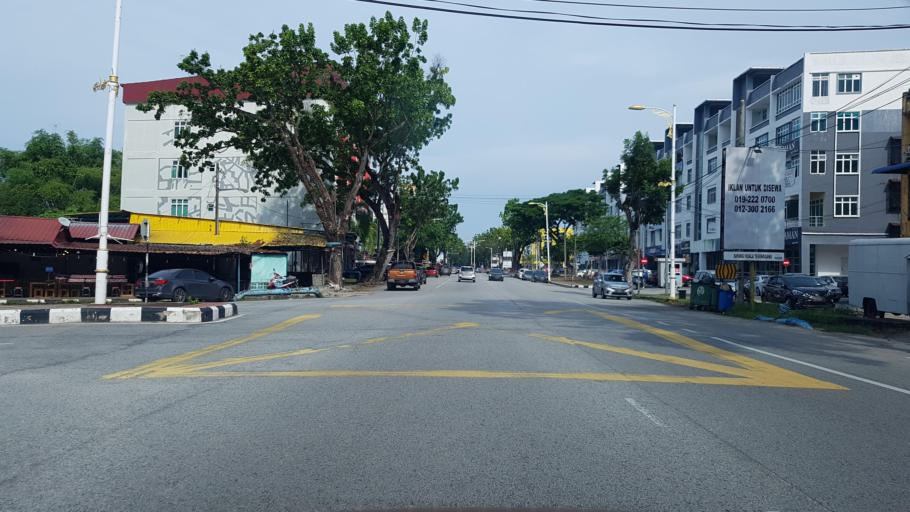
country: MY
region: Terengganu
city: Kuala Terengganu
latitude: 5.3333
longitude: 103.1417
